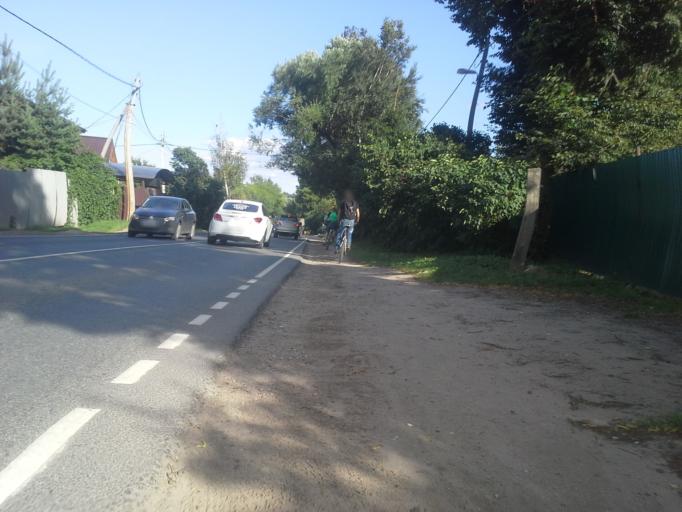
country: RU
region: Moskovskaya
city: Troitsk
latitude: 55.5026
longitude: 37.2826
